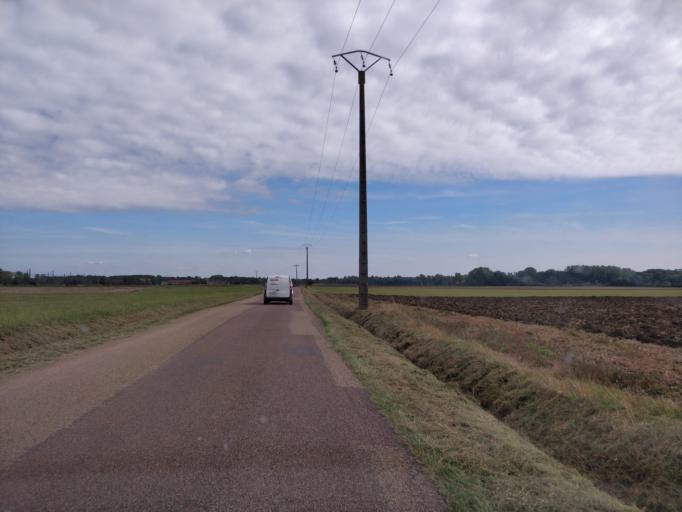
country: FR
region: Bourgogne
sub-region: Departement de l'Yonne
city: Brienon-sur-Armancon
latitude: 47.9804
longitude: 3.6320
